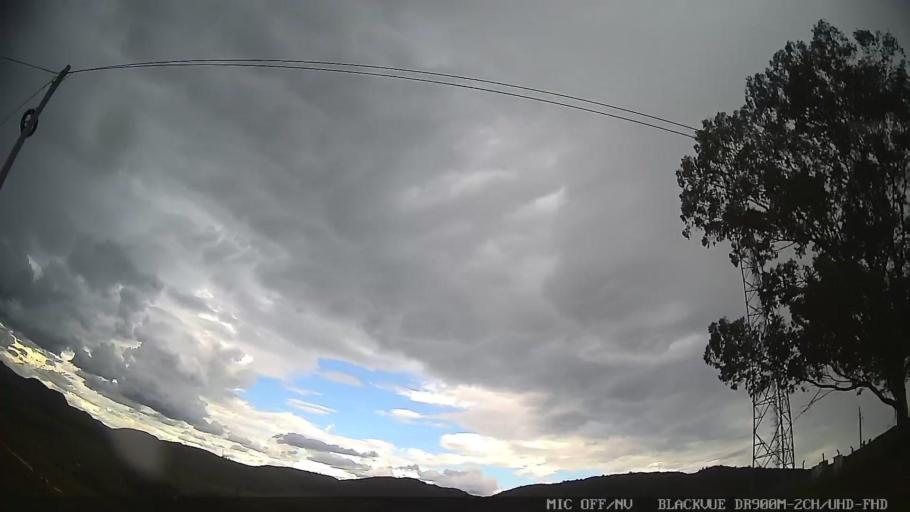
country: BR
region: Sao Paulo
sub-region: Pedreira
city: Pedreira
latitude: -22.7039
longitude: -46.8861
